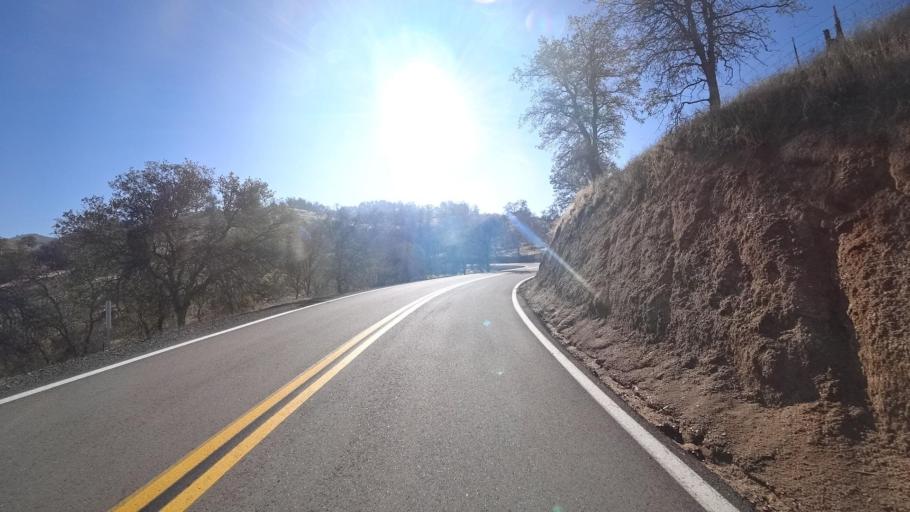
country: US
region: California
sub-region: Kern County
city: Alta Sierra
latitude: 35.7205
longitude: -118.7993
